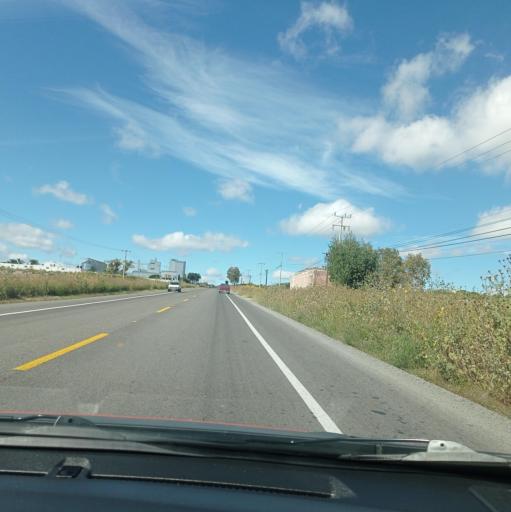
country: MX
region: Jalisco
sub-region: San Julian
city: Colonia Veintitres de Mayo
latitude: 21.0113
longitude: -102.2136
